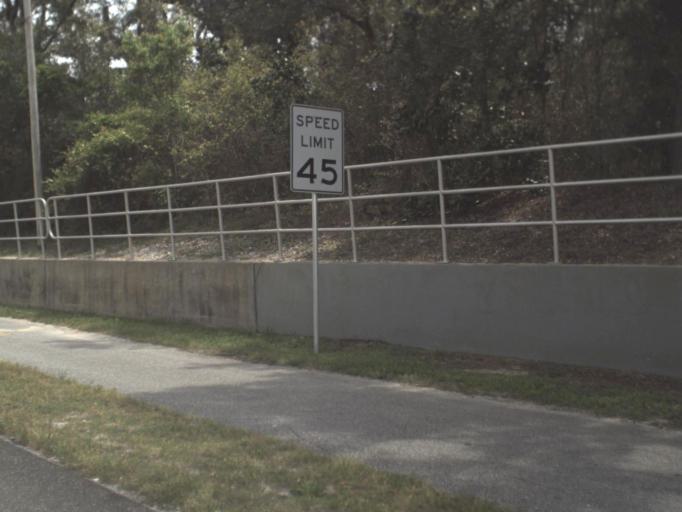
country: US
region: Florida
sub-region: Santa Rosa County
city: Gulf Breeze
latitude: 30.3644
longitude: -87.1340
